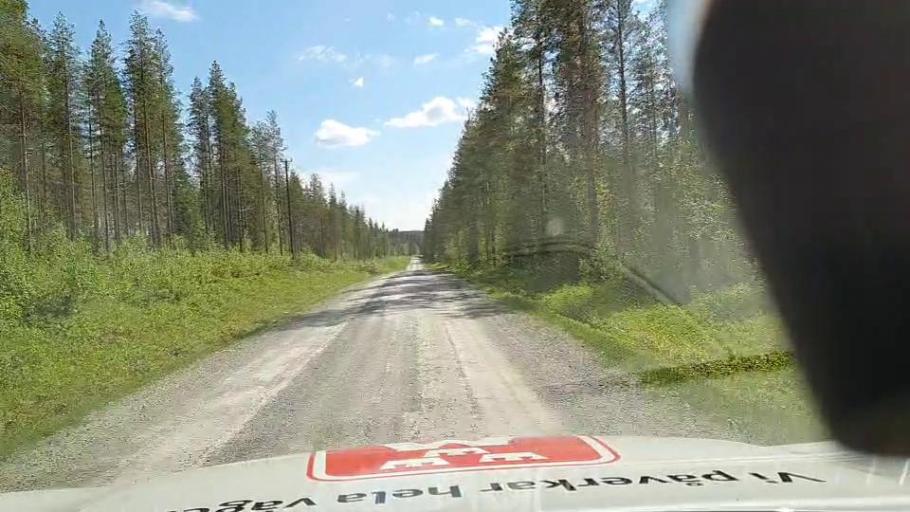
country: SE
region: Jaemtland
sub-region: Stroemsunds Kommun
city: Stroemsund
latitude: 64.4723
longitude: 15.5939
